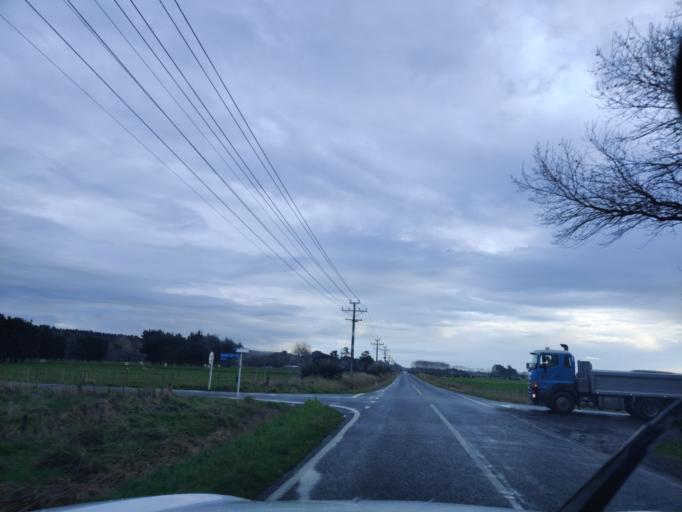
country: NZ
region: Manawatu-Wanganui
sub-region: Palmerston North City
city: Palmerston North
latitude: -40.3486
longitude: 175.7023
